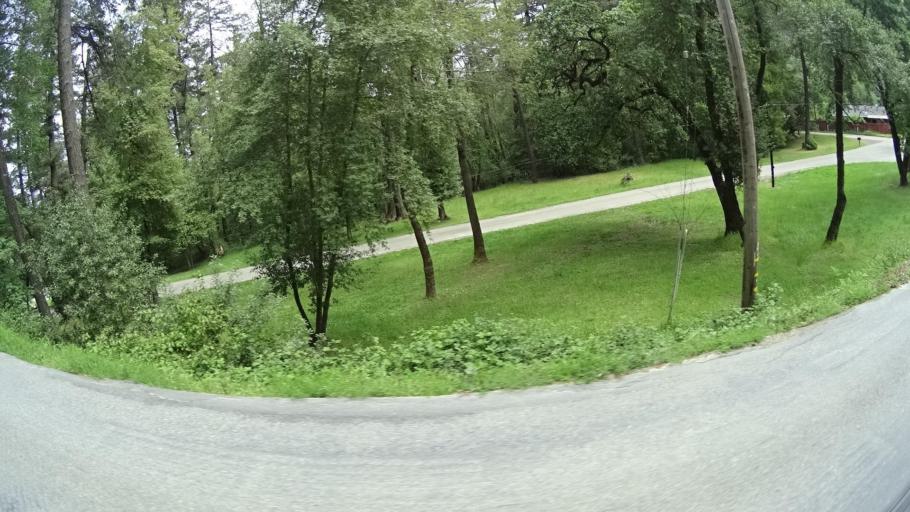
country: US
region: California
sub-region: Humboldt County
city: Redway
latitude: 40.0924
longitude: -123.8004
